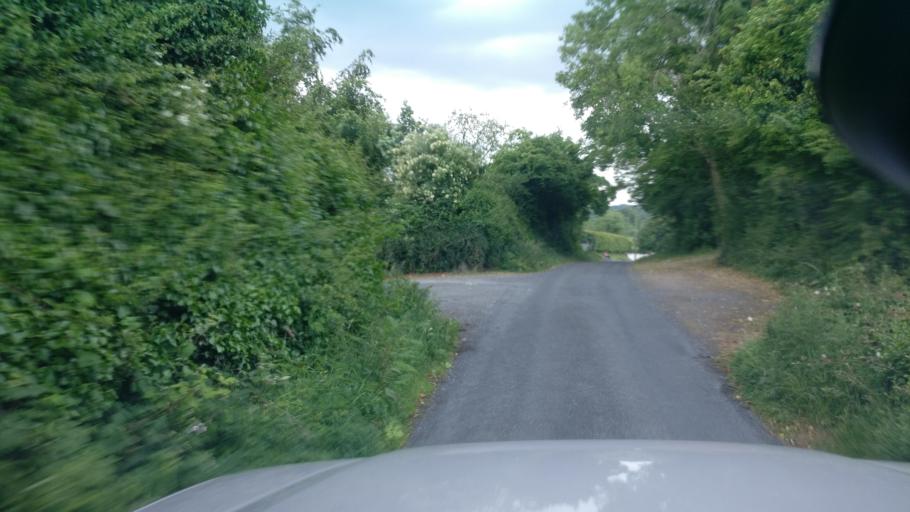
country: IE
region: Connaught
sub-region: County Galway
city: Ballinasloe
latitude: 53.3078
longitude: -8.2719
